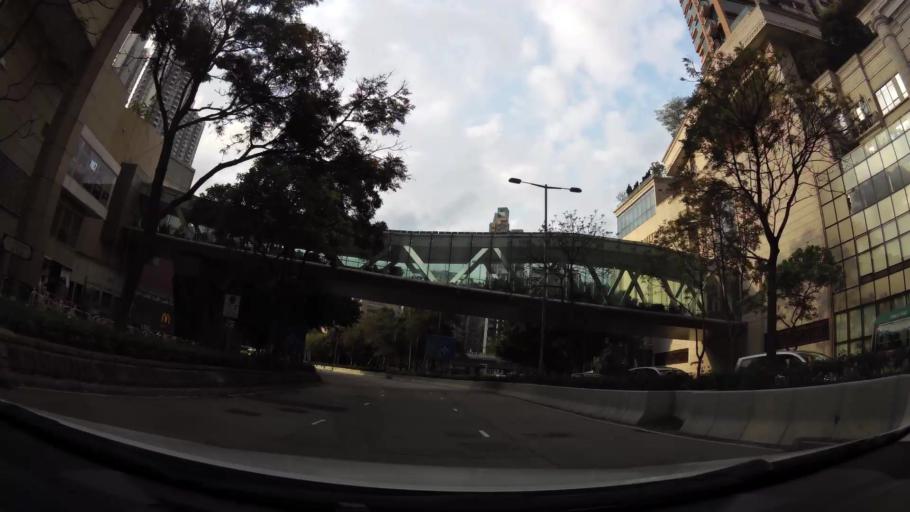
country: HK
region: Sham Shui Po
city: Sham Shui Po
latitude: 22.3172
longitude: 114.1635
